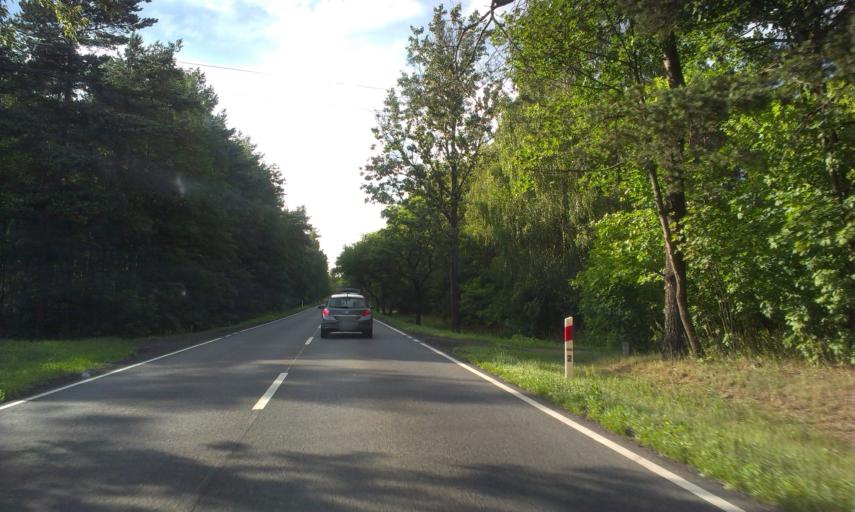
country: PL
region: Greater Poland Voivodeship
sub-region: Powiat zlotowski
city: Okonek
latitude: 53.4953
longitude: 16.8600
